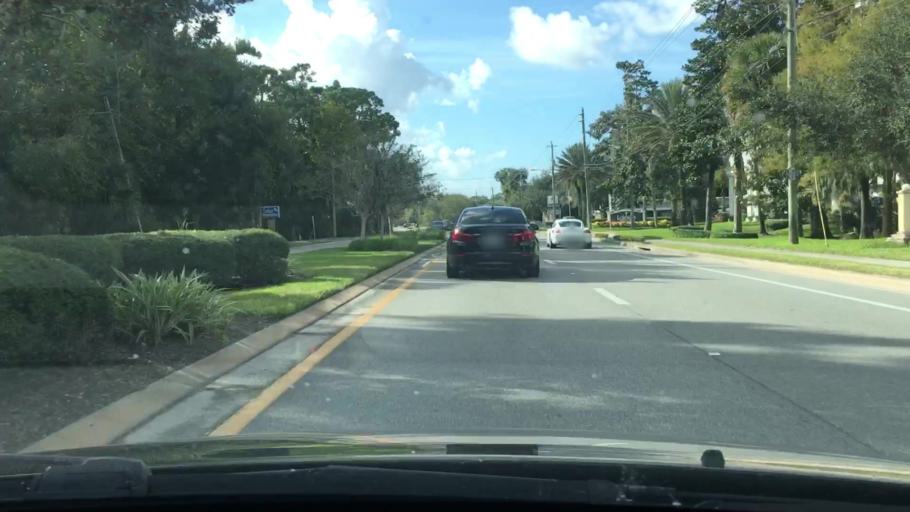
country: US
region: Florida
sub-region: Volusia County
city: Ormond Beach
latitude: 29.2788
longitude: -81.0765
